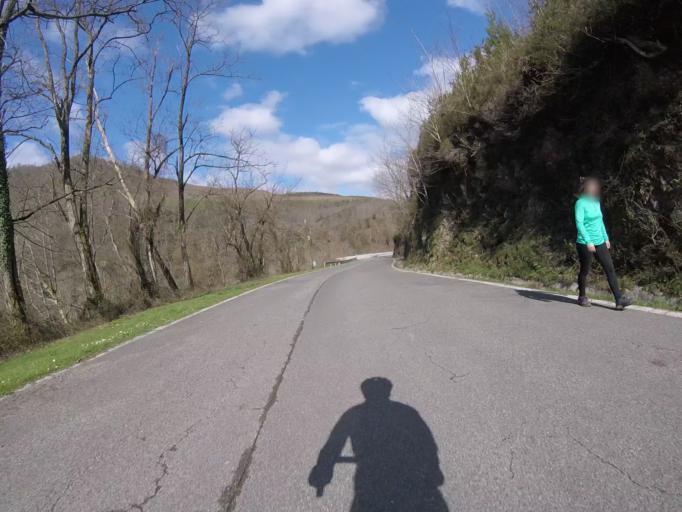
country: ES
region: Navarre
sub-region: Provincia de Navarra
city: Goizueta
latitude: 43.1516
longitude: -1.8500
